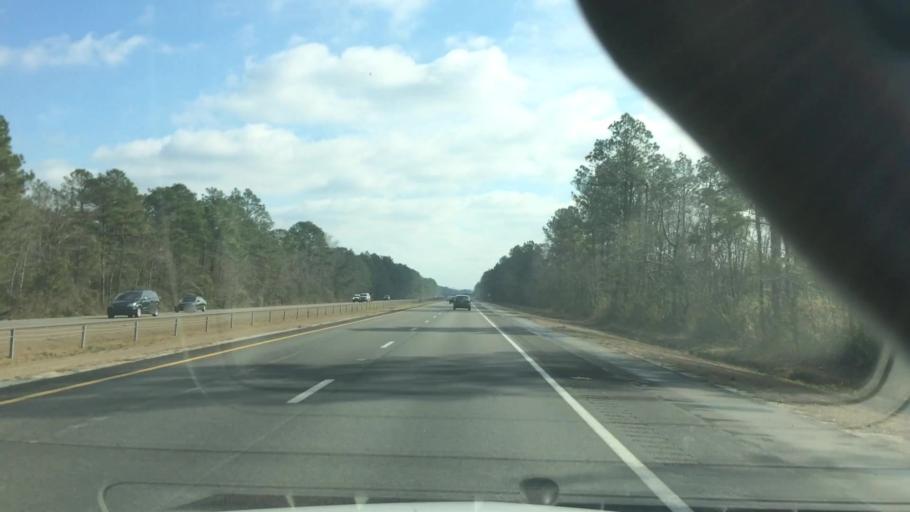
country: US
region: North Carolina
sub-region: Pender County
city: Burgaw
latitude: 34.6215
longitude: -77.9303
